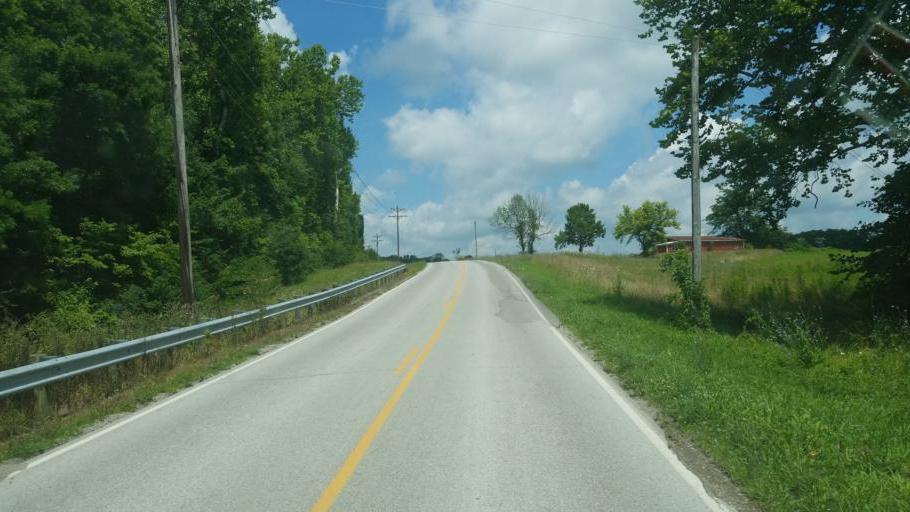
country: US
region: Ohio
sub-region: Highland County
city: Leesburg
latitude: 39.2652
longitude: -83.4738
